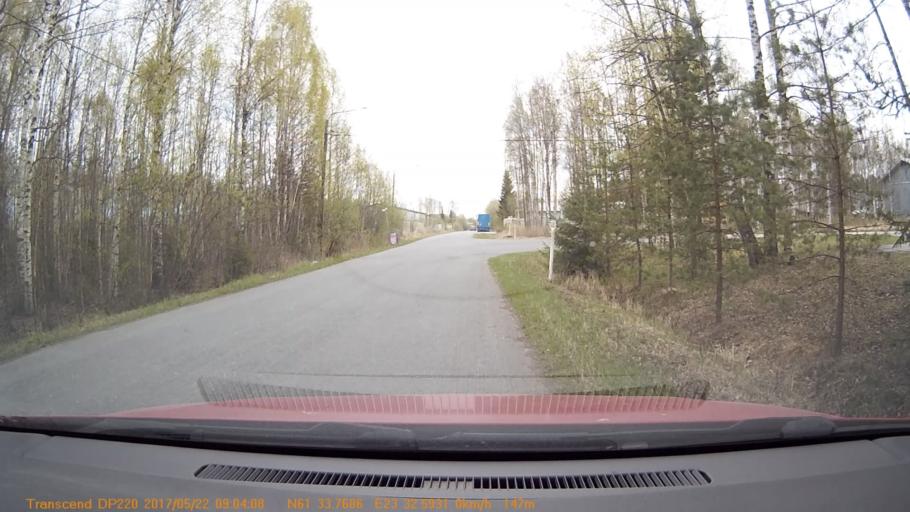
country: FI
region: Pirkanmaa
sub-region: Tampere
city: Yloejaervi
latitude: 61.5628
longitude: 23.5432
